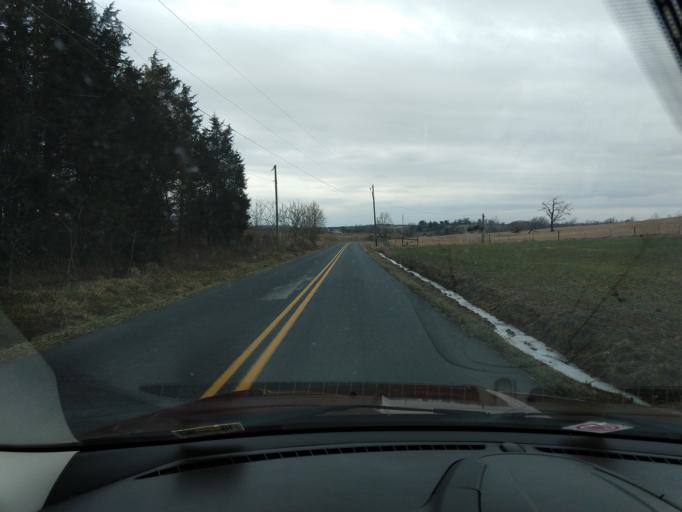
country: US
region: Virginia
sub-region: Augusta County
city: Weyers Cave
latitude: 38.2282
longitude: -78.8834
